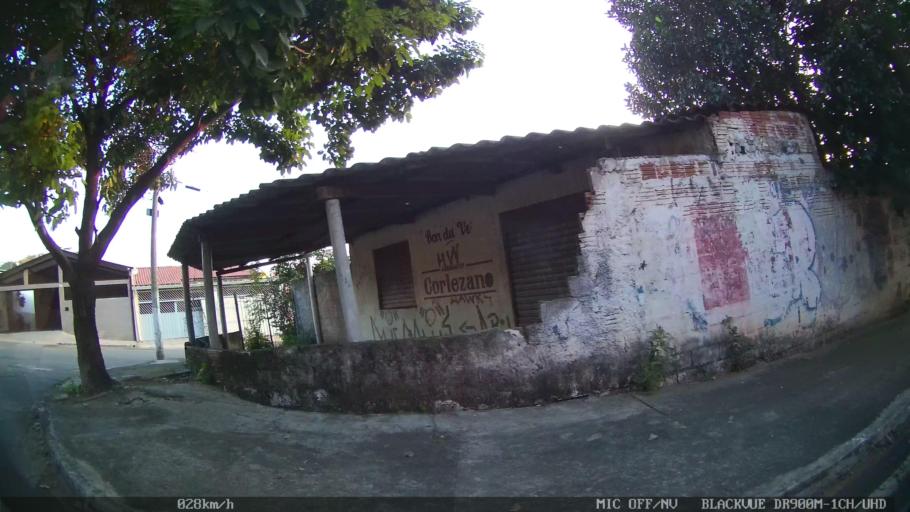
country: BR
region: Sao Paulo
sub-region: Campinas
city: Campinas
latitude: -22.9781
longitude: -47.1226
